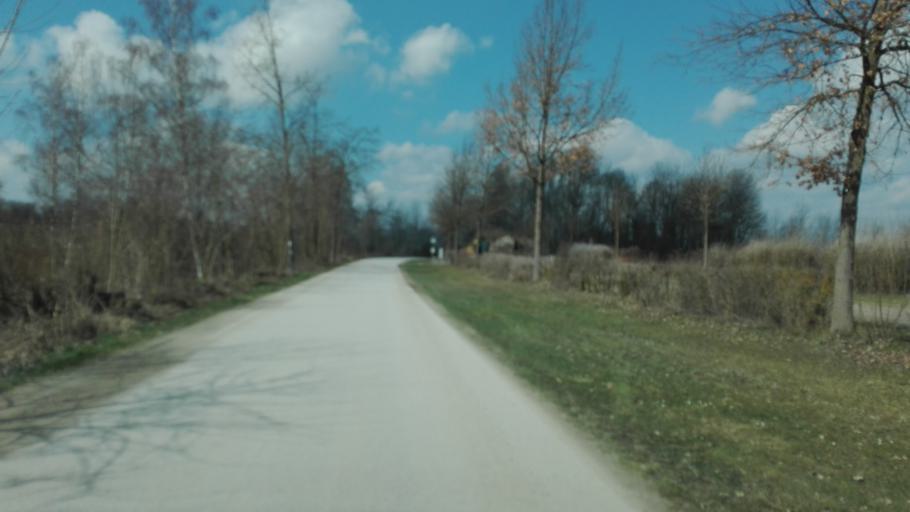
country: AT
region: Upper Austria
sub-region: Politischer Bezirk Urfahr-Umgebung
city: Feldkirchen an der Donau
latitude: 48.3213
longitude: 14.0678
